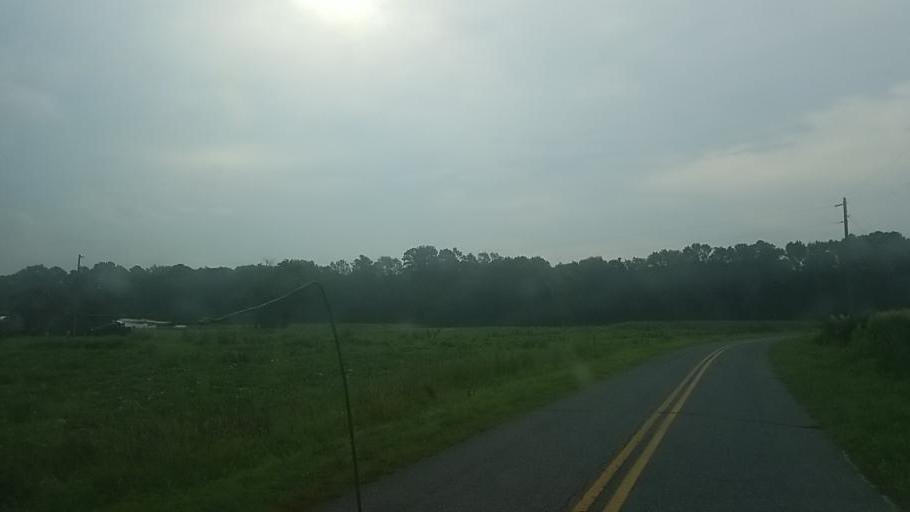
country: US
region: Maryland
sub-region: Wicomico County
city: Pittsville
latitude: 38.4333
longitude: -75.3244
